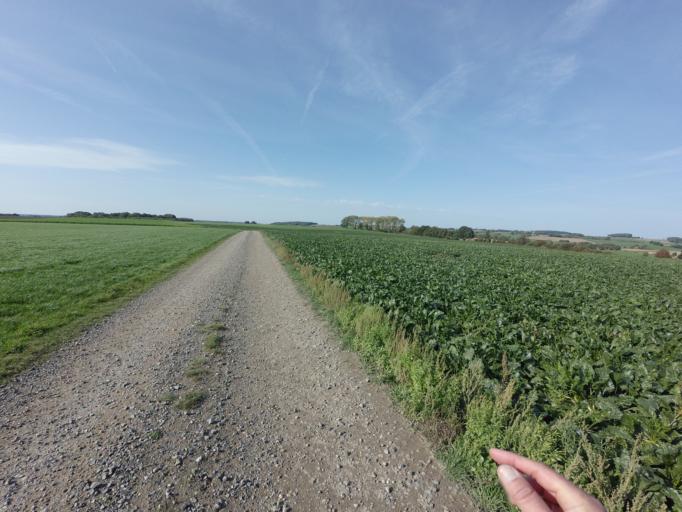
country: NL
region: Limburg
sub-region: Gemeente Simpelveld
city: Simpelveld
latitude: 50.8168
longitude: 5.9686
